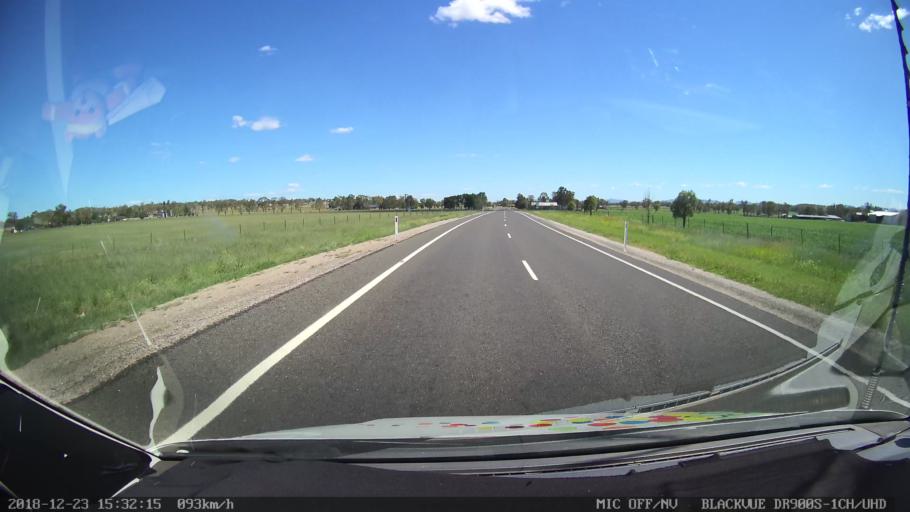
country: AU
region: New South Wales
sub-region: Tamworth Municipality
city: East Tamworth
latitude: -30.9830
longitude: 150.8702
